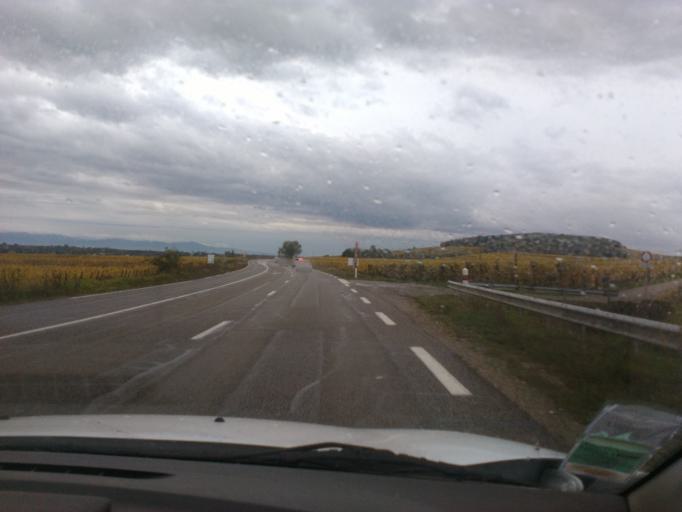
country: FR
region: Alsace
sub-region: Departement du Haut-Rhin
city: Ammerschwihr
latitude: 48.1161
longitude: 7.2900
